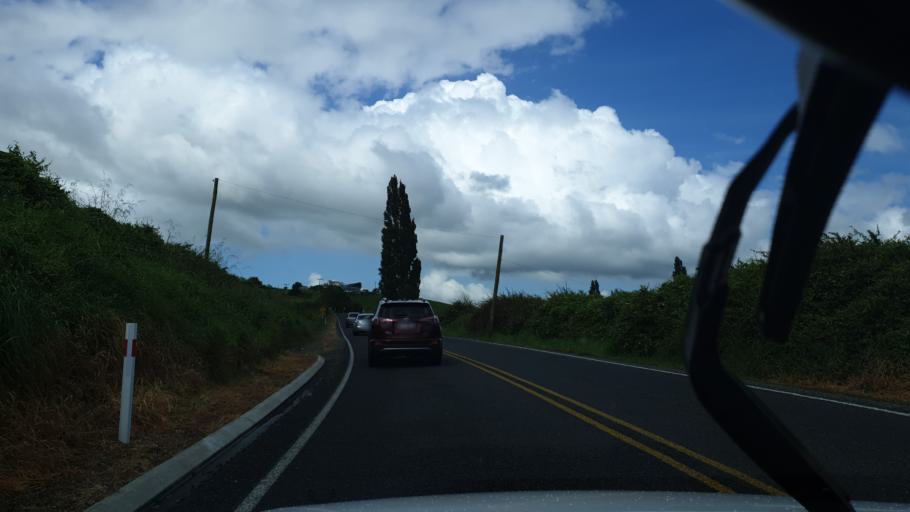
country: NZ
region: Waikato
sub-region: Matamata-Piako District
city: Matamata
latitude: -37.8776
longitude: 175.6991
